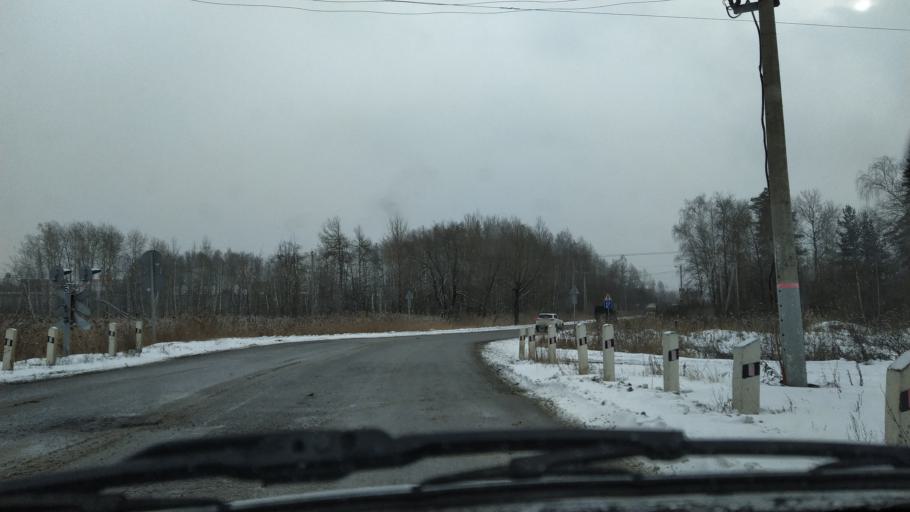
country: RU
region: Moskovskaya
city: Lopatinskiy
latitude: 55.3567
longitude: 38.7378
